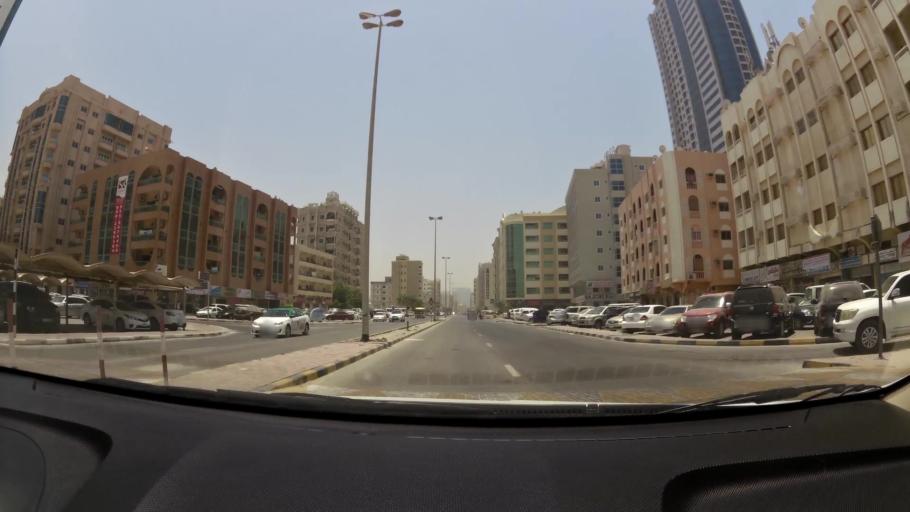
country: AE
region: Ajman
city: Ajman
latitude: 25.4170
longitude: 55.4408
